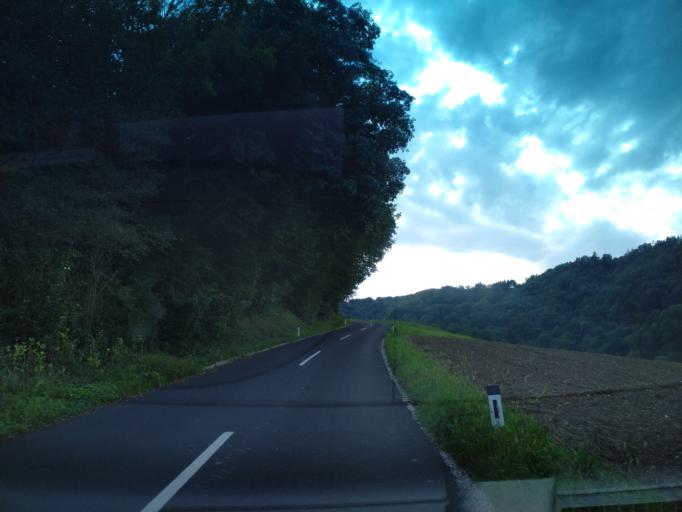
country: AT
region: Styria
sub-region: Politischer Bezirk Leibnitz
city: Kaindorf an der Sulm
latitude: 46.7886
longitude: 15.5237
